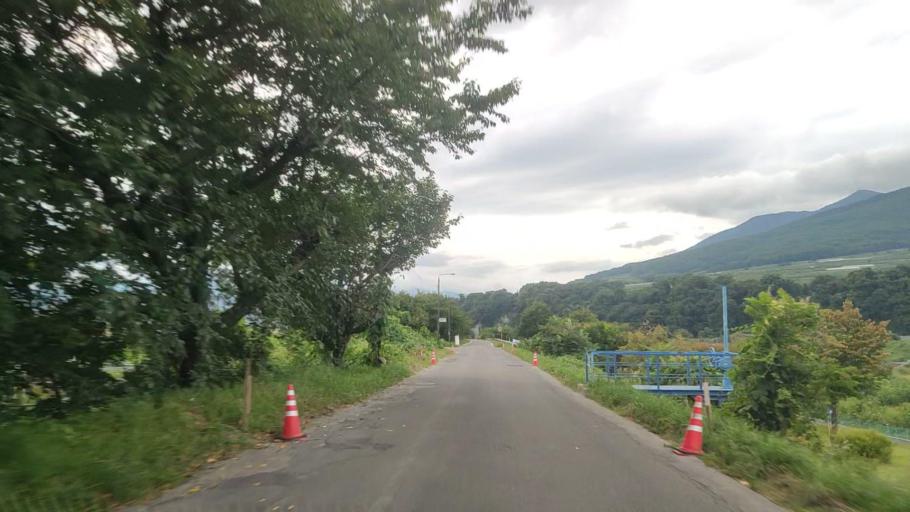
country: JP
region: Nagano
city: Nakano
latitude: 36.7655
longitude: 138.3937
